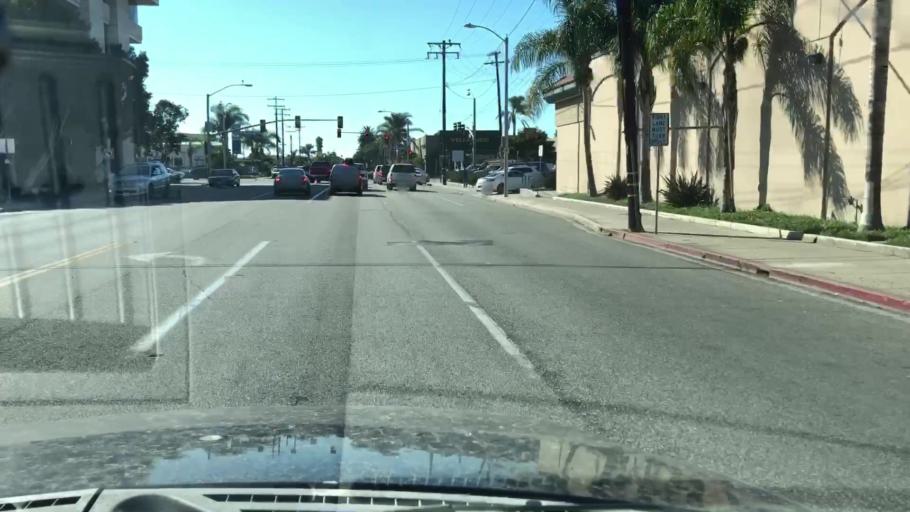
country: US
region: California
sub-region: Ventura County
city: Oxnard
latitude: 34.1734
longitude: -119.1764
